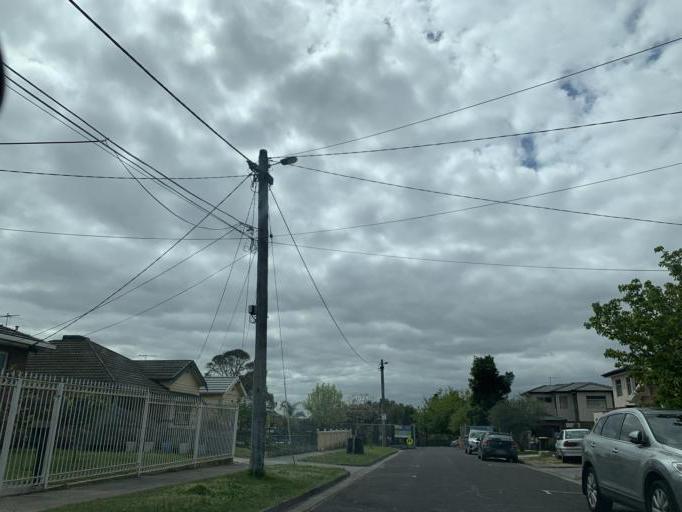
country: AU
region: Victoria
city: Thornbury
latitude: -37.7386
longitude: 144.9929
